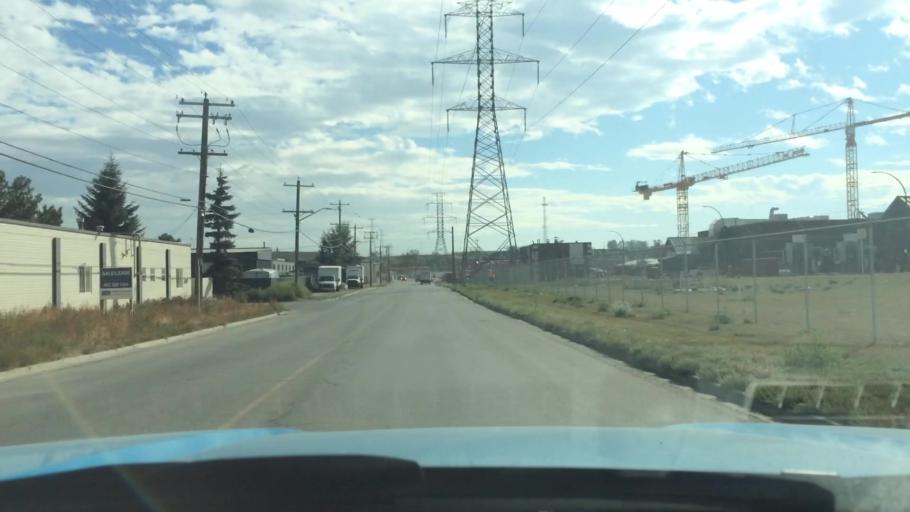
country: CA
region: Alberta
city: Calgary
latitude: 51.0155
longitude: -114.0201
